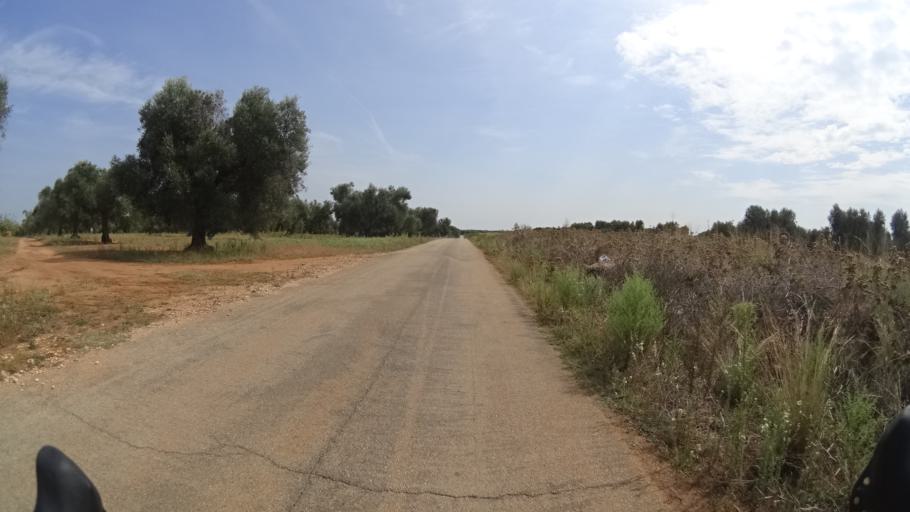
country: IT
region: Apulia
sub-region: Provincia di Lecce
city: Porto Cesareo
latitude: 40.3239
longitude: 17.8937
